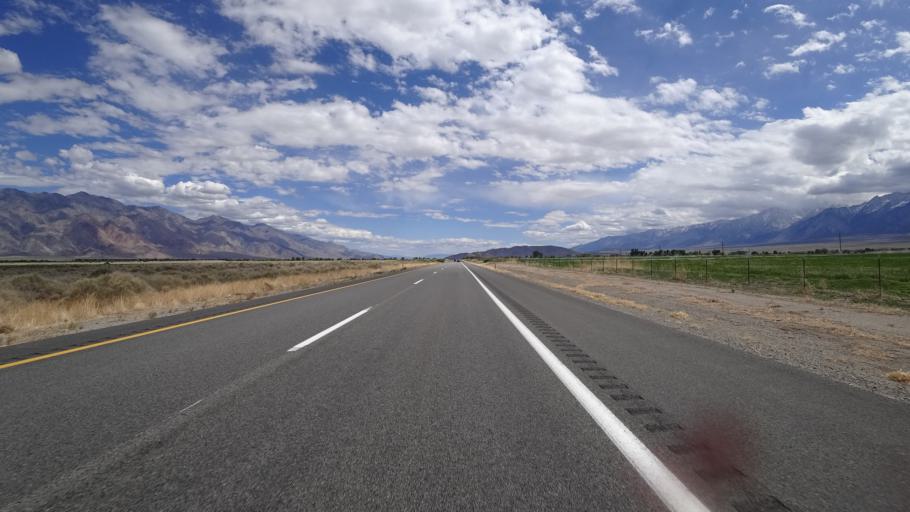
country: US
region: California
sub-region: Inyo County
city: Lone Pine
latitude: 36.7518
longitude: -118.1579
